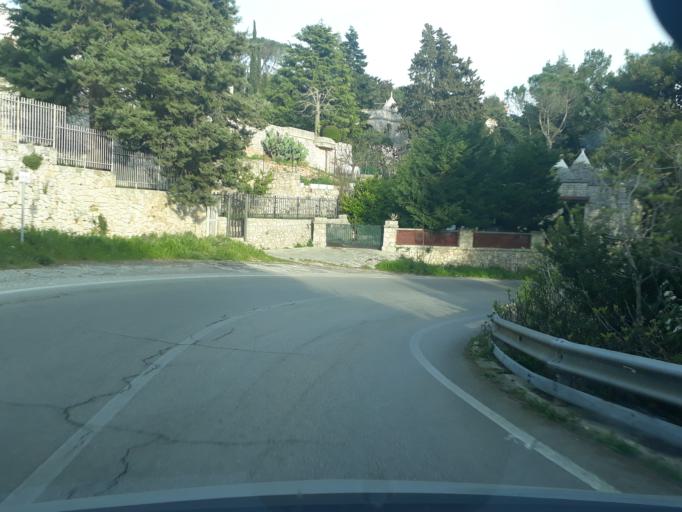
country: IT
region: Apulia
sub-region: Provincia di Brindisi
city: Lamie di Olimpie-Selva
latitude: 40.8227
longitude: 17.3267
